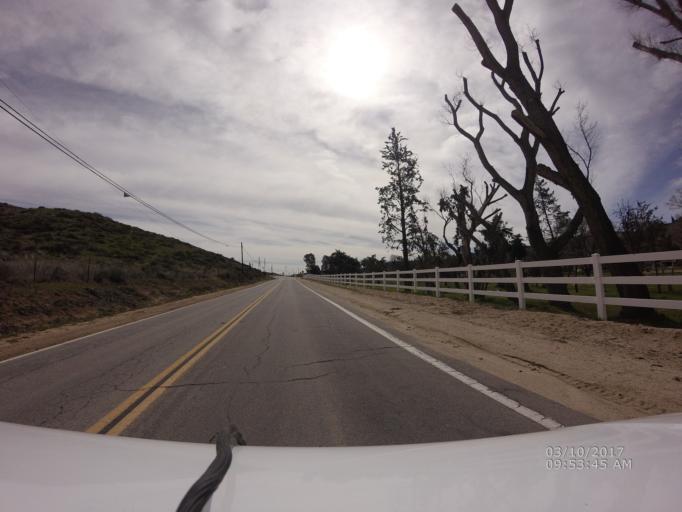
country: US
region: California
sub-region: Los Angeles County
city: Green Valley
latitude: 34.6608
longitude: -118.3796
